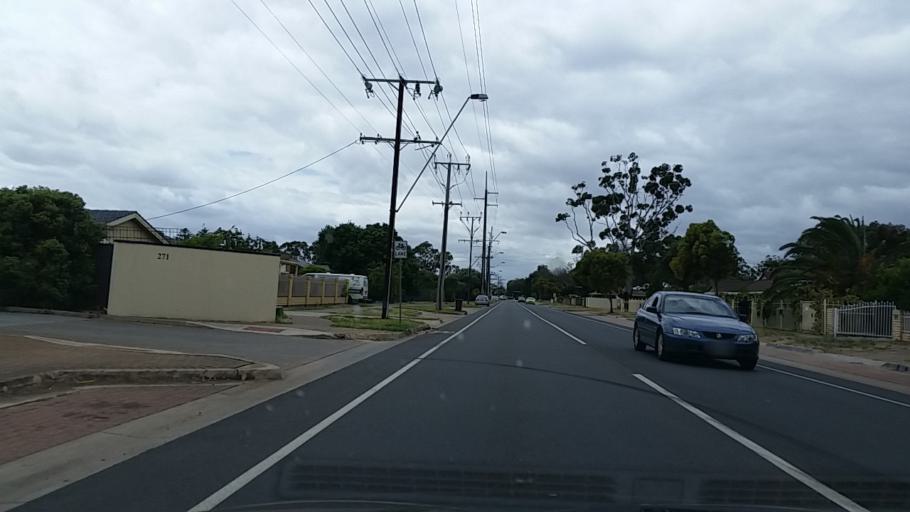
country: AU
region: South Australia
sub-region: Salisbury
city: Salisbury
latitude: -34.7839
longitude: 138.6063
